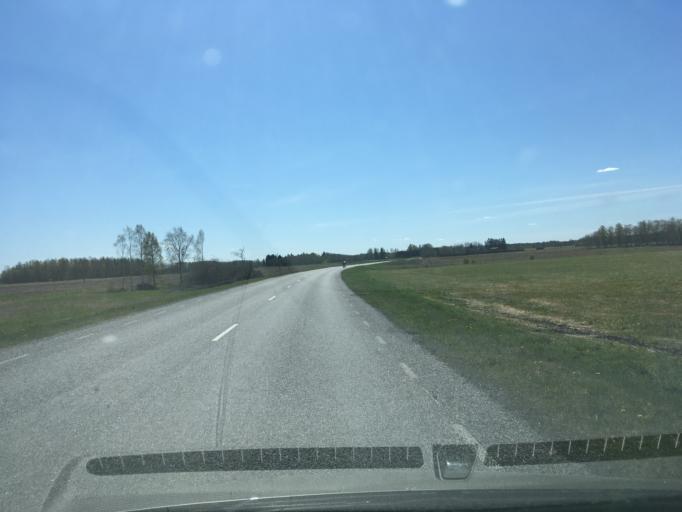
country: EE
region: Harju
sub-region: Raasiku vald
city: Arukula
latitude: 59.4180
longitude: 25.0785
